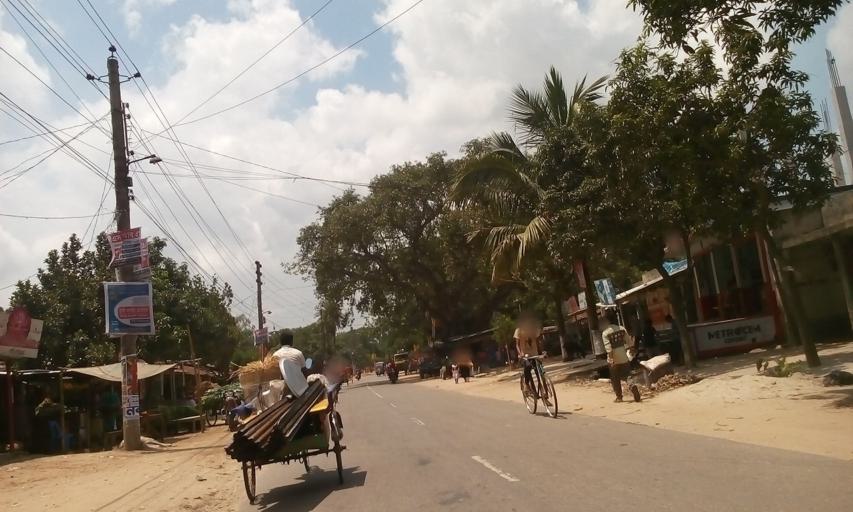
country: IN
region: West Bengal
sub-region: Dakshin Dinajpur
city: Balurghat
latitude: 25.3788
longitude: 88.9913
